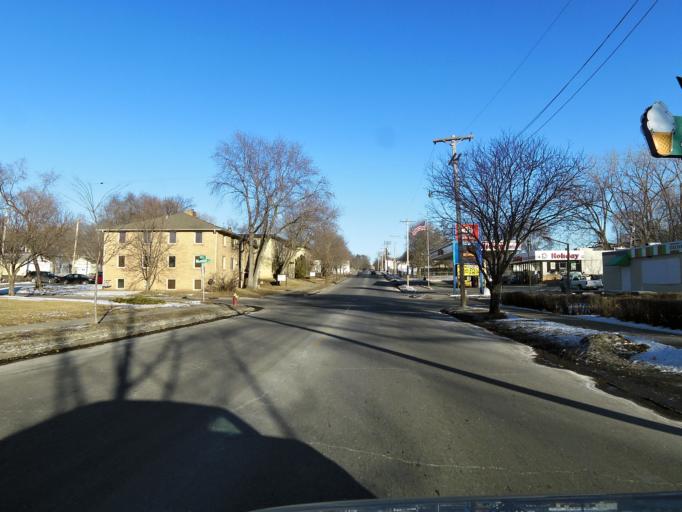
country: US
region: Minnesota
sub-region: Ramsey County
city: Maplewood
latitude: 44.9631
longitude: -93.0402
